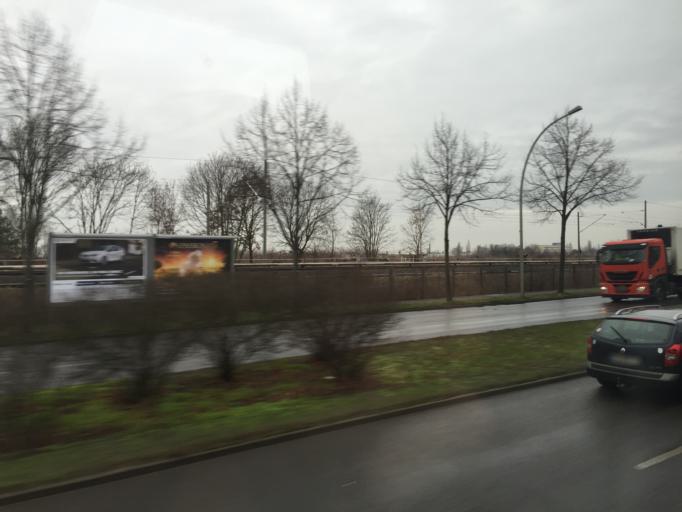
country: DE
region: Berlin
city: Adlershof
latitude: 52.4414
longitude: 13.5327
